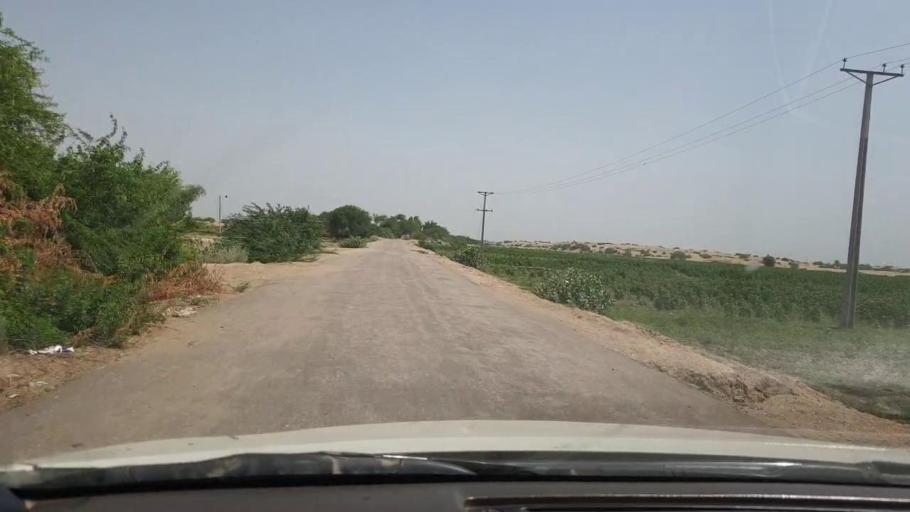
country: PK
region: Sindh
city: Rohri
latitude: 27.5020
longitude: 69.0416
